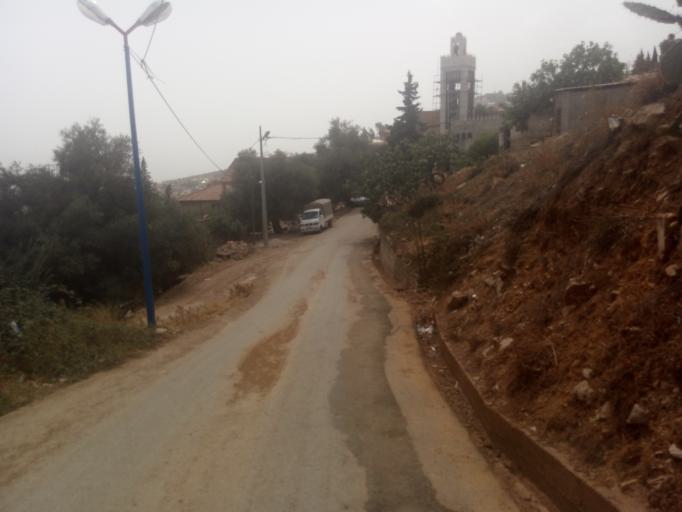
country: DZ
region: Tizi Ouzou
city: Chemini
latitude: 36.6031
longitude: 4.6380
